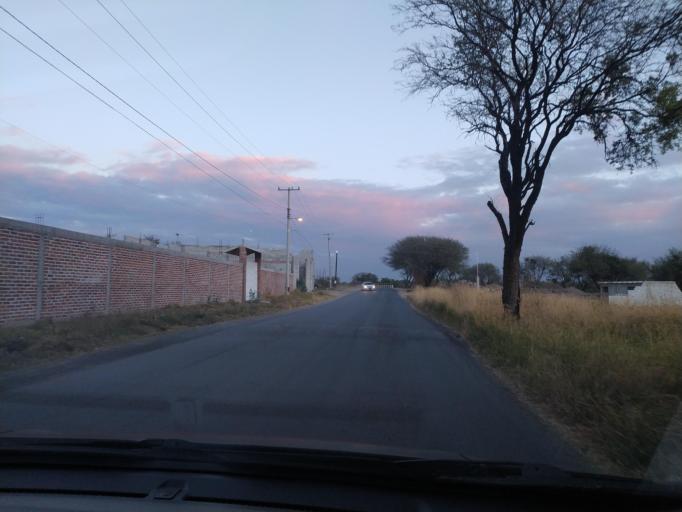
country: MX
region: Guanajuato
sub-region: San Francisco del Rincon
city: San Roque de Montes
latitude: 21.0167
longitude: -101.8200
